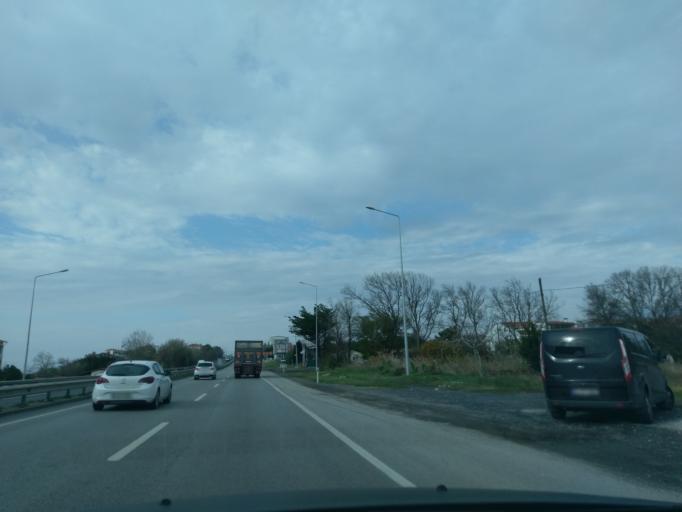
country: TR
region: Istanbul
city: Celaliye
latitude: 41.0480
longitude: 28.3995
